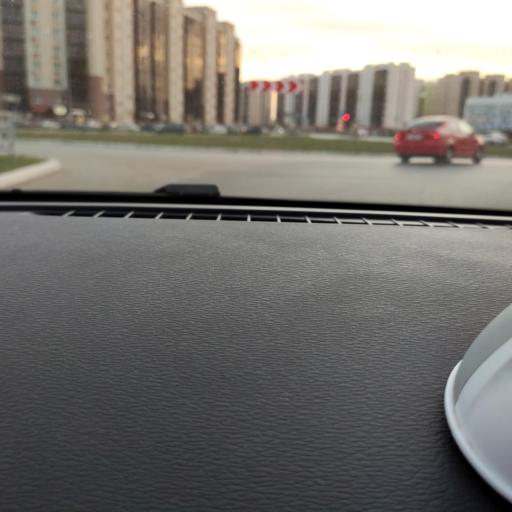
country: RU
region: Samara
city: Samara
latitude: 53.1124
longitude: 50.1437
